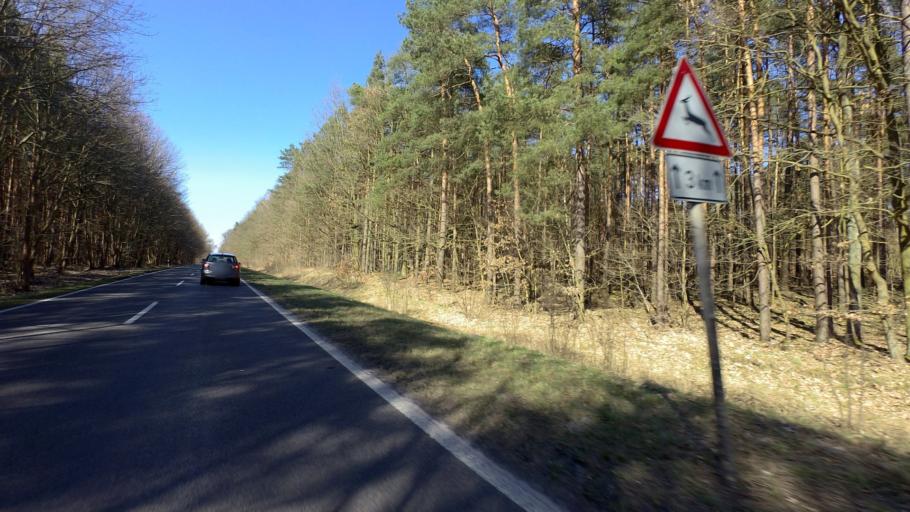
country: DE
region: Brandenburg
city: Eberswalde
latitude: 52.7887
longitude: 13.8385
